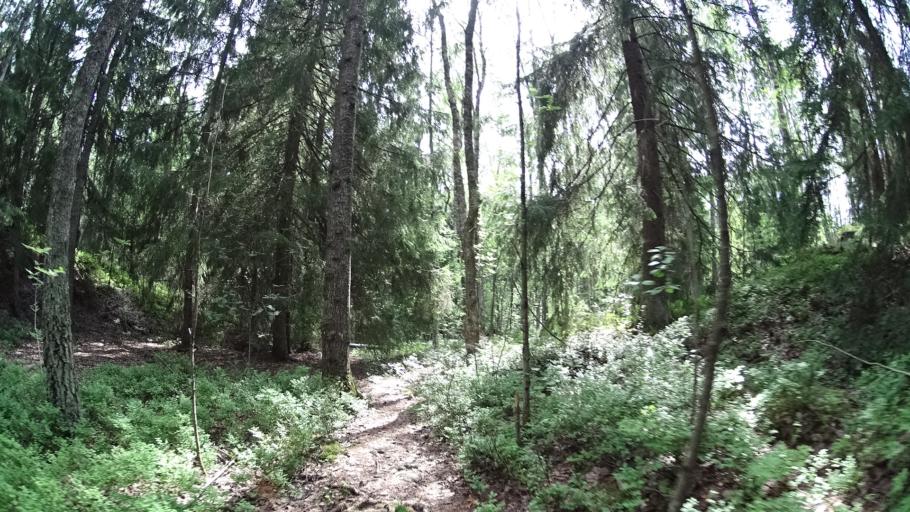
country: FI
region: Uusimaa
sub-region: Helsinki
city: Kauniainen
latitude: 60.1961
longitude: 24.7242
